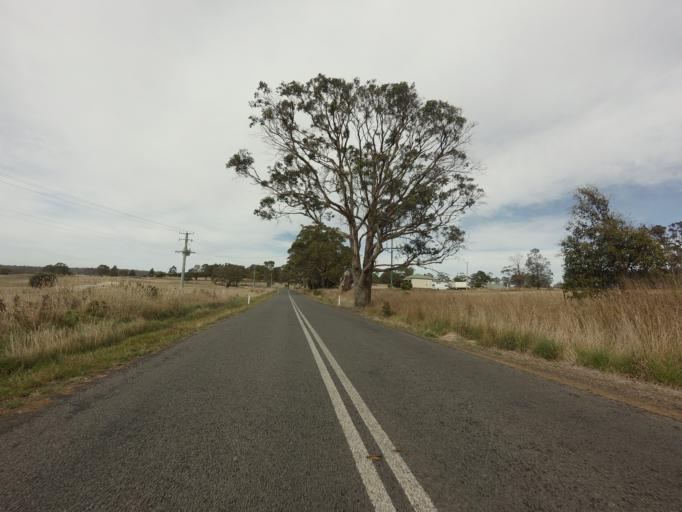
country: AU
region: Tasmania
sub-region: Brighton
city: Bridgewater
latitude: -42.3843
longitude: 147.4227
